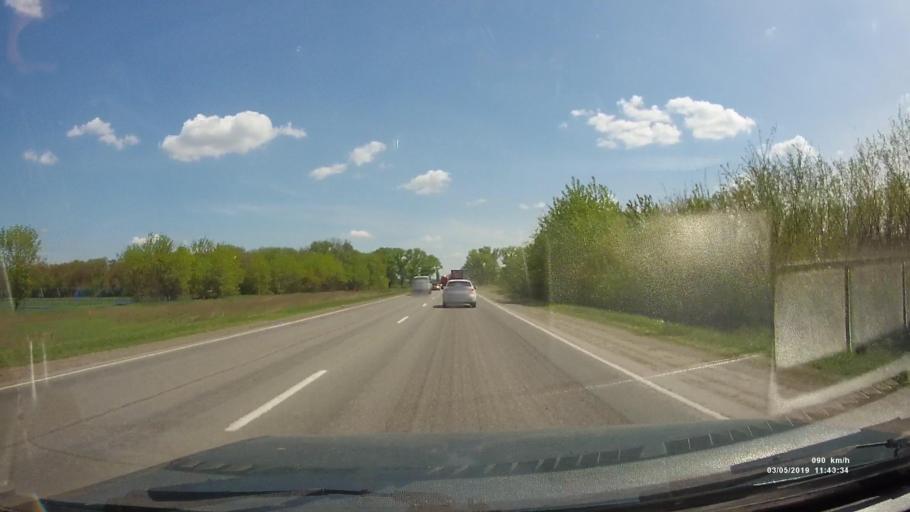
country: RU
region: Rostov
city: Starocherkasskaya
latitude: 47.1404
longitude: 40.0660
